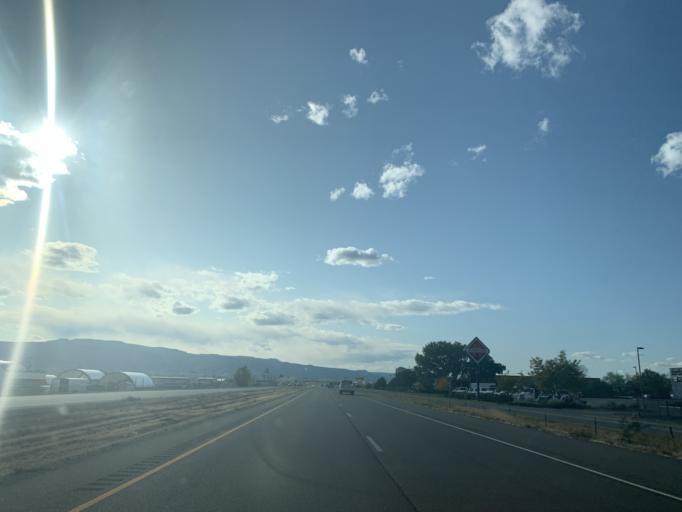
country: US
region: Colorado
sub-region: Mesa County
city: Redlands
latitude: 39.1140
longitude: -108.6180
